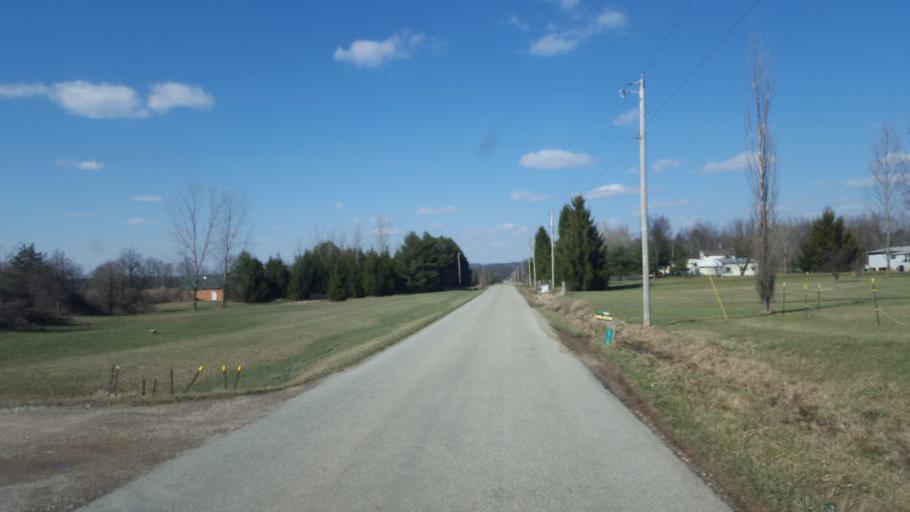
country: US
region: Ohio
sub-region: Knox County
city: Centerburg
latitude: 40.4441
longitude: -82.6782
